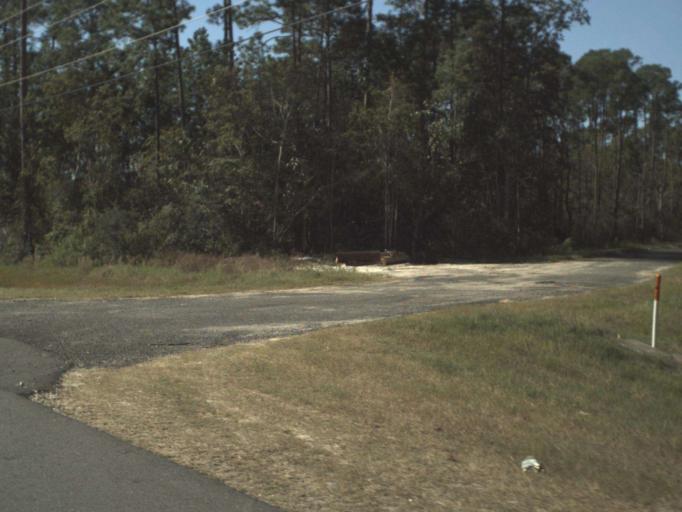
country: US
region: Florida
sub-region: Walton County
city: Freeport
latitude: 30.4606
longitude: -86.1313
